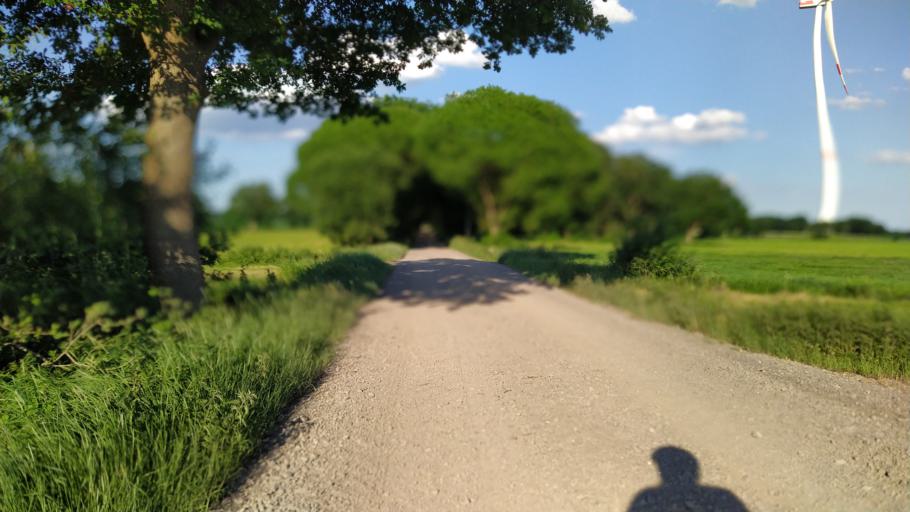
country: DE
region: Lower Saxony
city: Lintig
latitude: 53.5897
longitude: 8.9369
